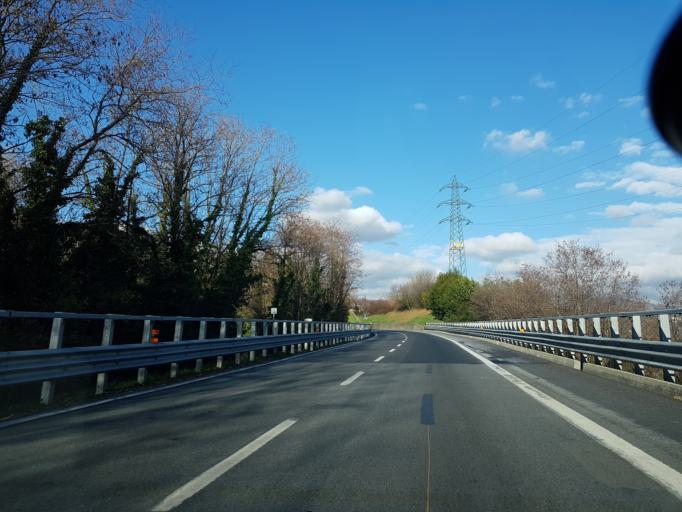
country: IT
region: Liguria
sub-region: Provincia di Genova
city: Pedemonte
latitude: 44.4915
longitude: 8.9176
